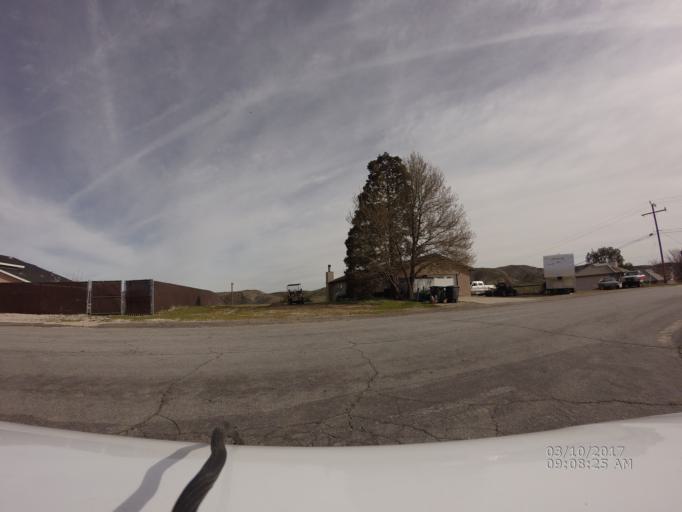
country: US
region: California
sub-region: Los Angeles County
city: Green Valley
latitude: 34.6575
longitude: -118.3864
